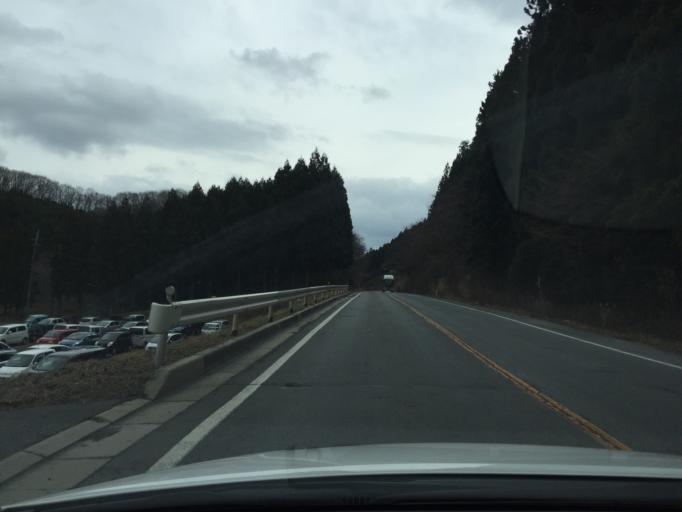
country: JP
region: Fukushima
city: Ishikawa
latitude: 37.1730
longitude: 140.6522
